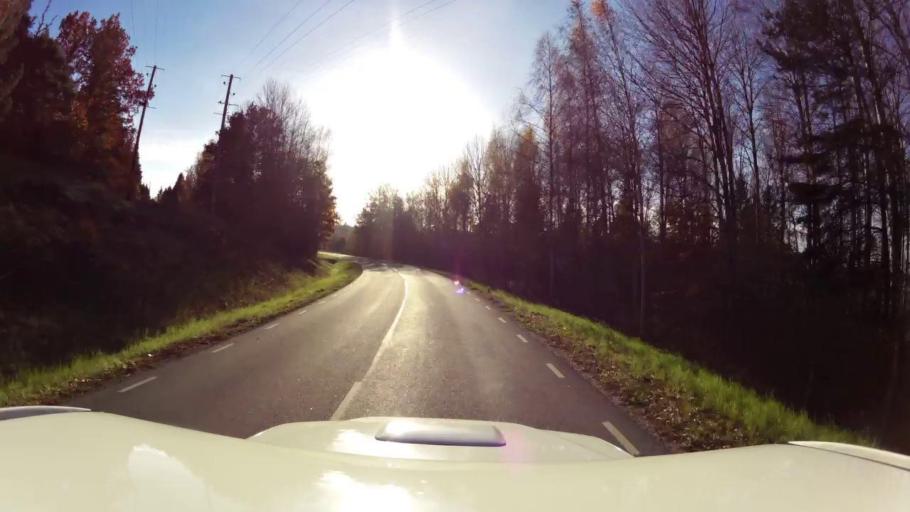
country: SE
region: OEstergoetland
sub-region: Linkopings Kommun
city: Vikingstad
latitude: 58.3002
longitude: 15.4694
